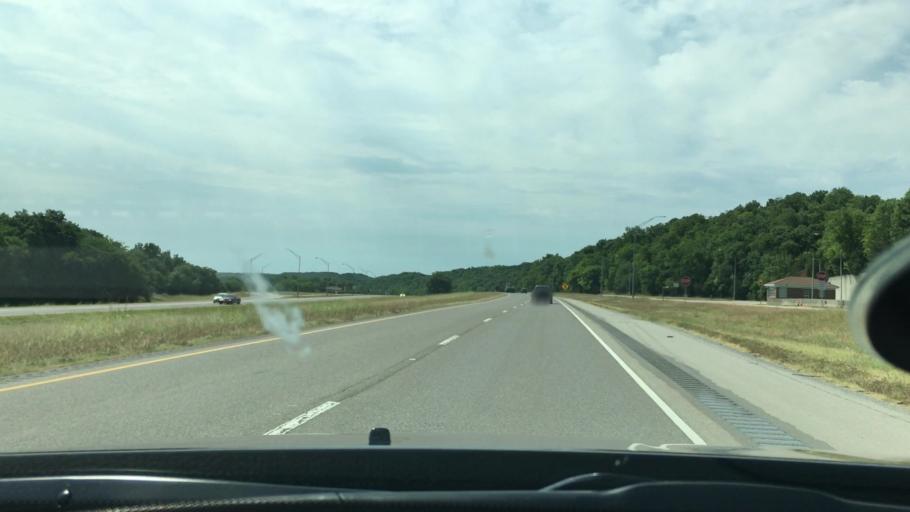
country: US
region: Oklahoma
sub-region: Murray County
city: Davis
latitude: 34.4788
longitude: -97.1575
